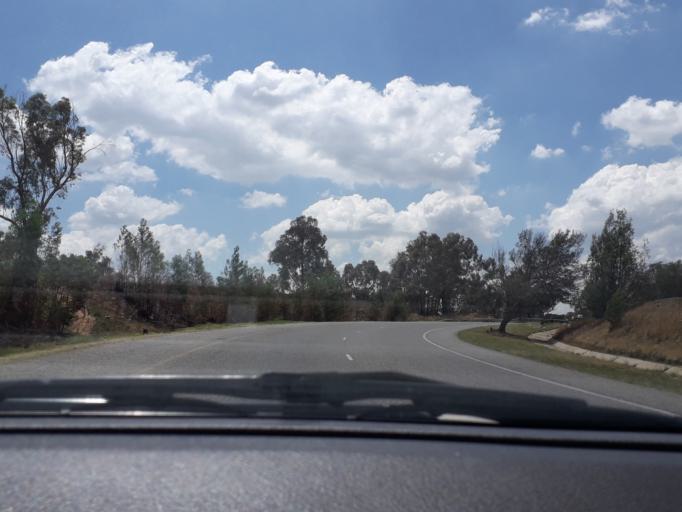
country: ZA
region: Gauteng
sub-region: City of Johannesburg Metropolitan Municipality
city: Johannesburg
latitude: -26.2604
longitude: 27.9813
